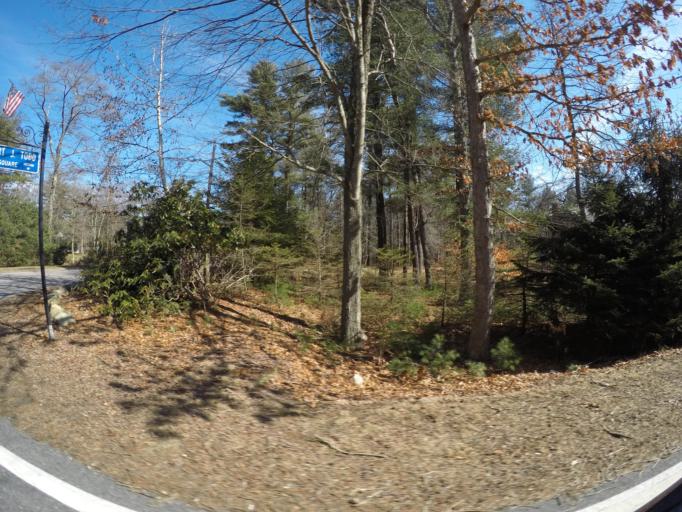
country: US
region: Massachusetts
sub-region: Bristol County
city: Easton
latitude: 42.0677
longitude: -71.1361
